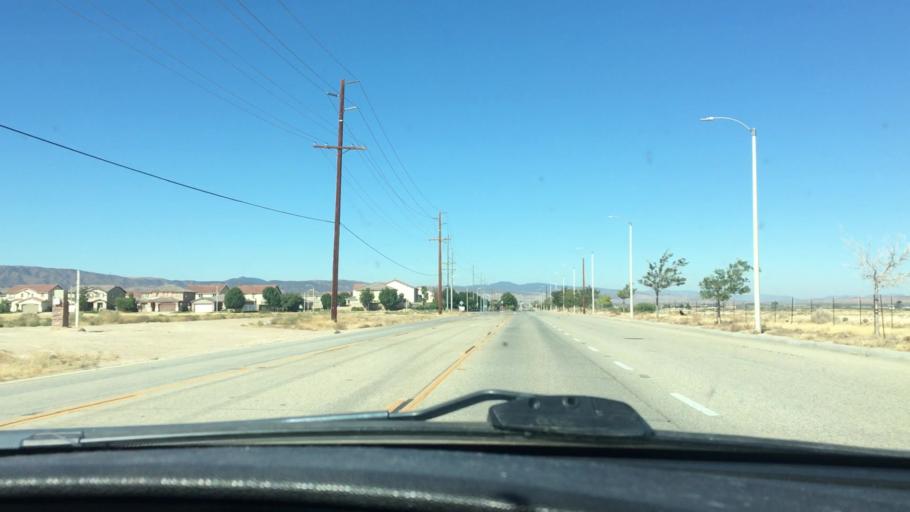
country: US
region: California
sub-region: Los Angeles County
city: Quartz Hill
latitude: 34.6894
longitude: -118.2298
